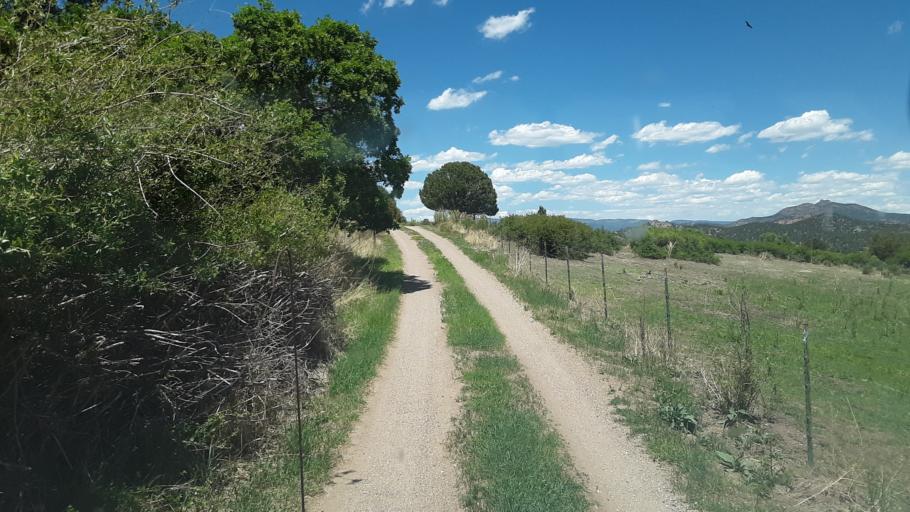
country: US
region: Colorado
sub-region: Custer County
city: Westcliffe
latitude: 38.2822
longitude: -105.6065
